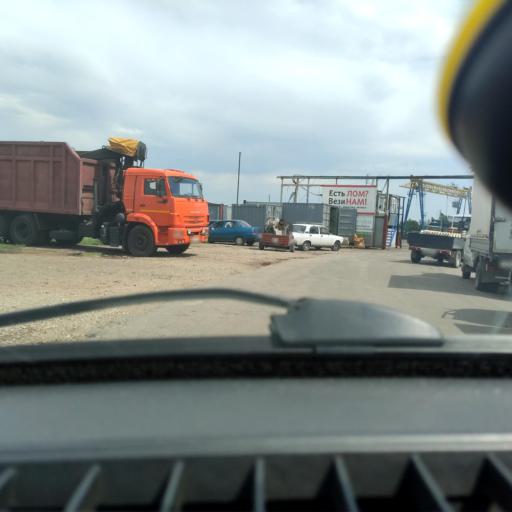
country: RU
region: Samara
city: Tol'yatti
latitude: 53.5608
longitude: 49.3445
